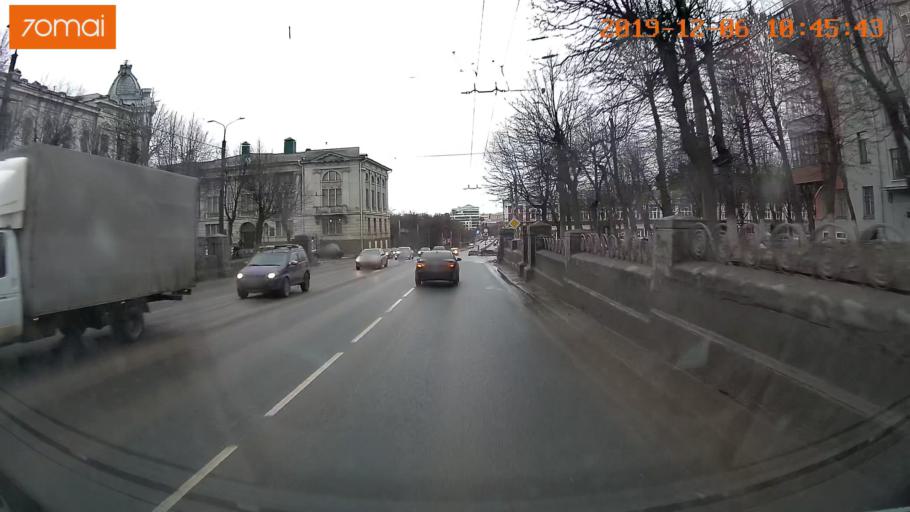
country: RU
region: Ivanovo
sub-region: Gorod Ivanovo
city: Ivanovo
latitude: 57.0051
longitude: 40.9732
